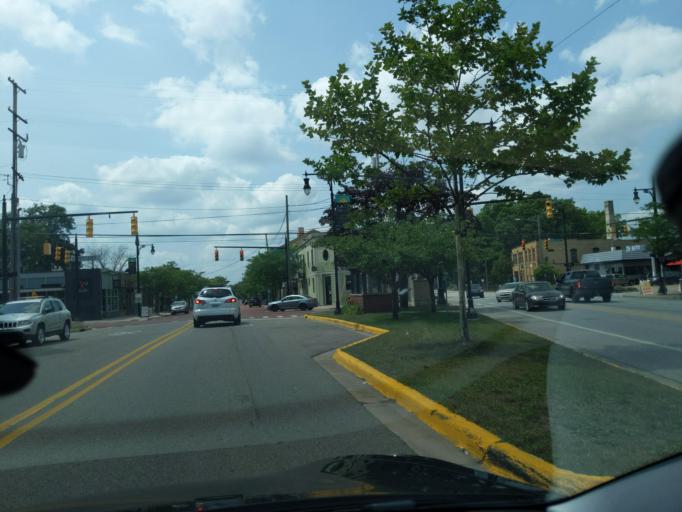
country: US
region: Michigan
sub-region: Kent County
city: Grand Rapids
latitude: 42.9596
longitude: -85.6439
